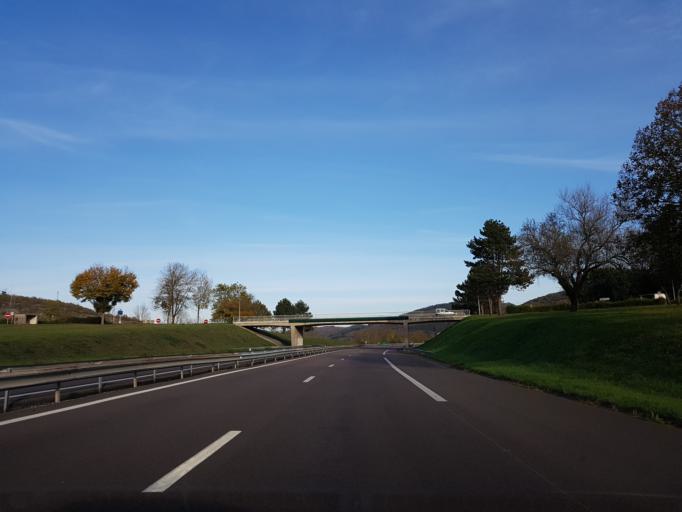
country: FR
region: Bourgogne
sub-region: Departement de la Cote-d'Or
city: Velars-sur-Ouche
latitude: 47.3185
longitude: 4.9135
